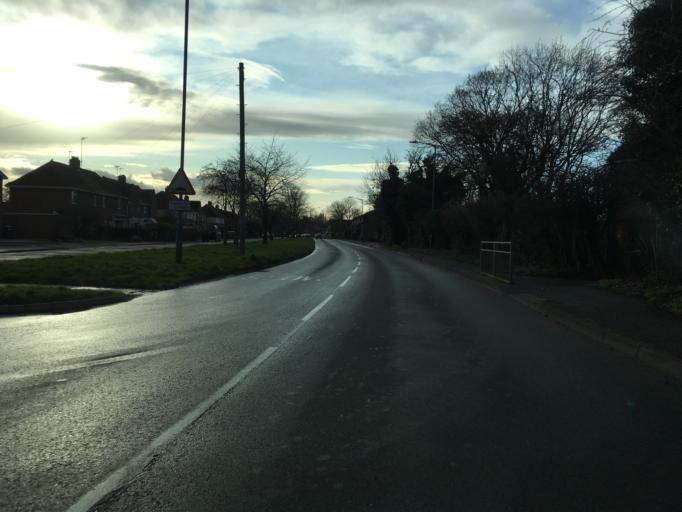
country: GB
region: England
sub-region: Warwickshire
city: Alcester
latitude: 52.2206
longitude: -1.8610
